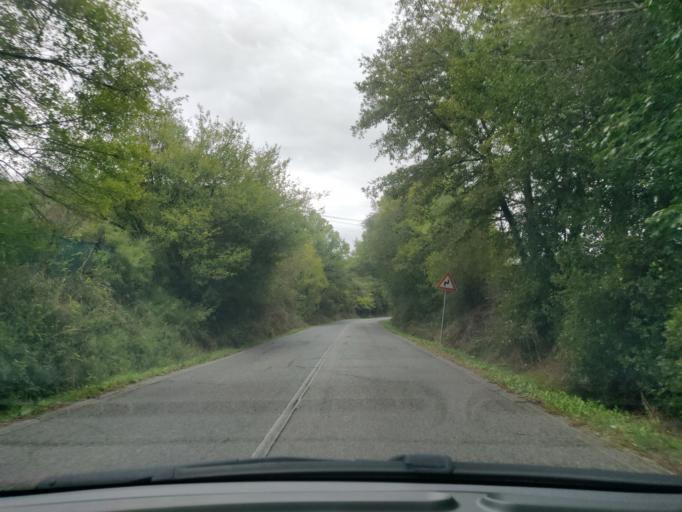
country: IT
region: Latium
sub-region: Citta metropolitana di Roma Capitale
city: Allumiere
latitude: 42.1299
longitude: 11.8665
